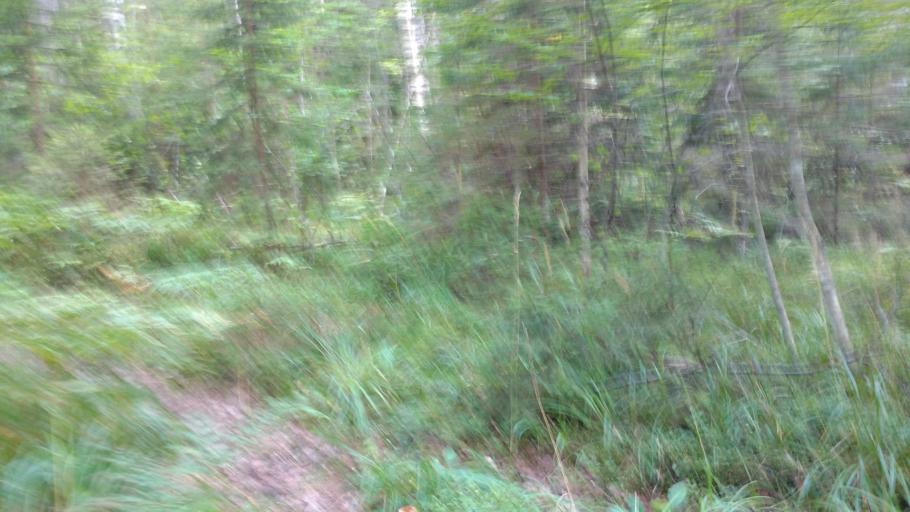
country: FI
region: Varsinais-Suomi
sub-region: Salo
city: Salo
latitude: 60.3610
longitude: 23.1675
